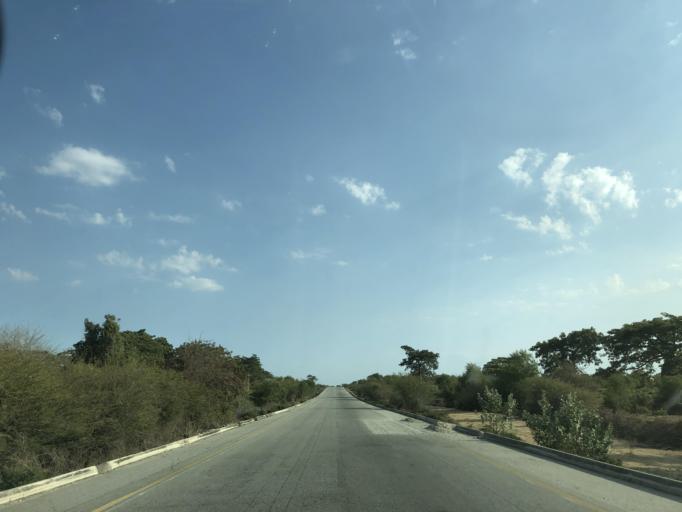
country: AO
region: Benguela
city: Benguela
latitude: -13.2027
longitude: 13.7634
